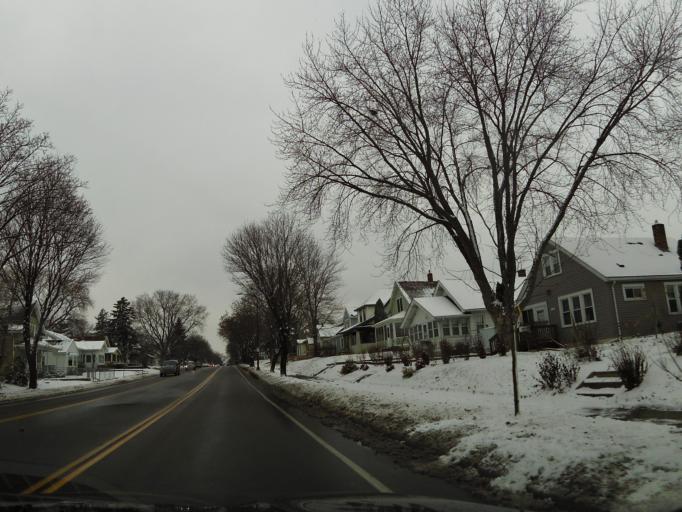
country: US
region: Minnesota
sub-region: Ramsey County
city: Saint Paul
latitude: 44.9776
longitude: -93.0511
